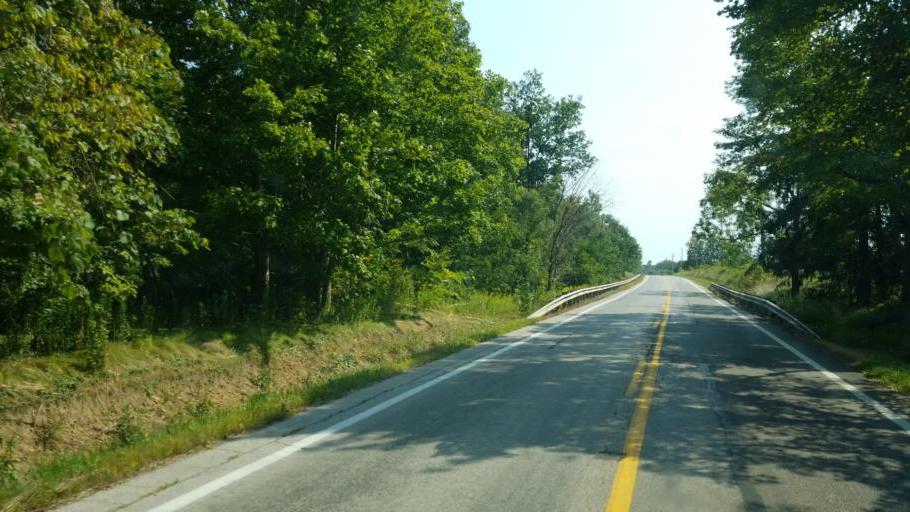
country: US
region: Ohio
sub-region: Ashtabula County
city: Orwell
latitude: 41.5634
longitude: -80.9875
